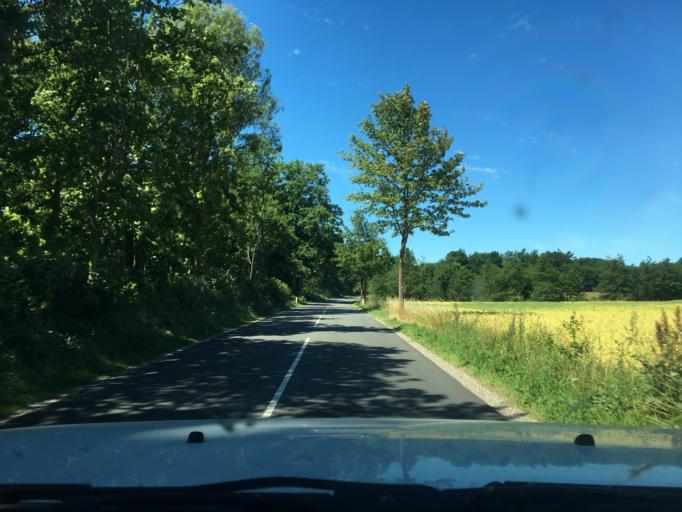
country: DK
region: Central Jutland
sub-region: Syddjurs Kommune
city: Hornslet
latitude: 56.3296
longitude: 10.3426
